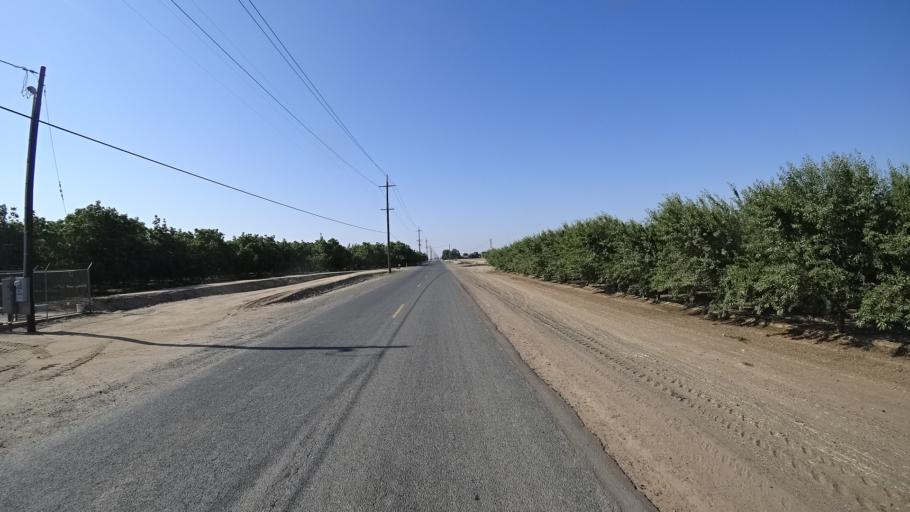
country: US
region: California
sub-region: Kings County
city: Home Garden
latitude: 36.2739
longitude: -119.5831
